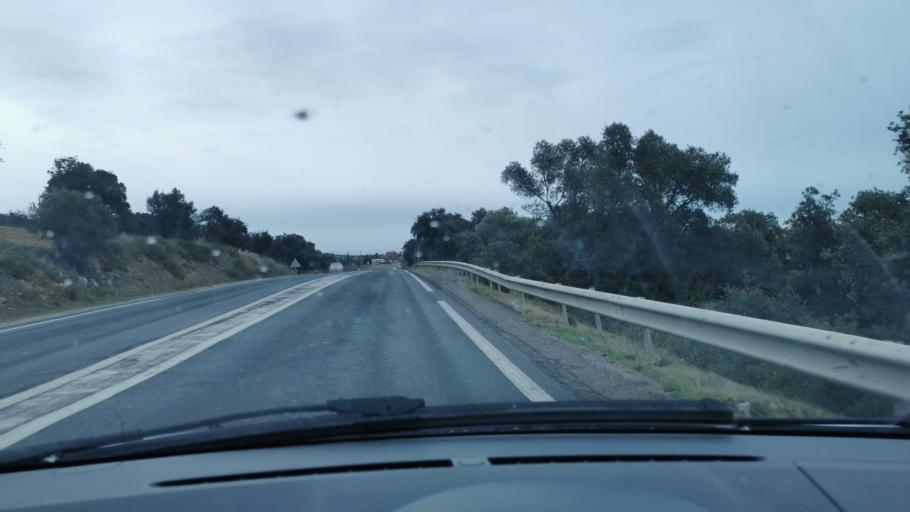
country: FR
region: Languedoc-Roussillon
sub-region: Departement de l'Herault
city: Vic-la-Gardiole
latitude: 43.4970
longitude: 3.7789
